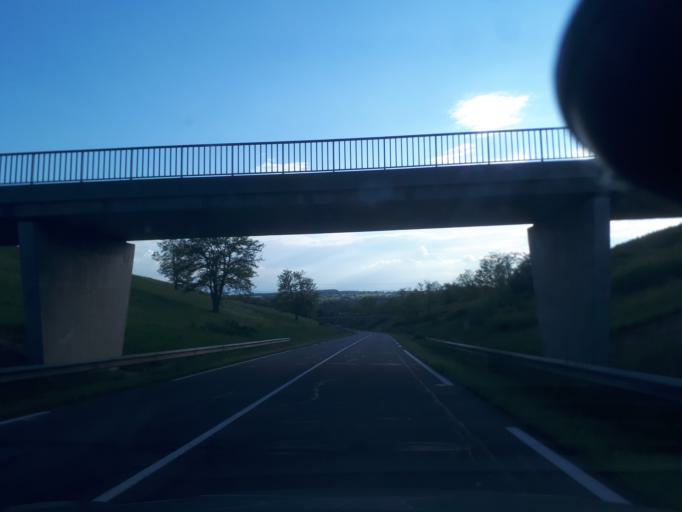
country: FR
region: Bourgogne
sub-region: Departement de Saone-et-Loire
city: Marcigny
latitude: 46.2871
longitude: 4.0369
